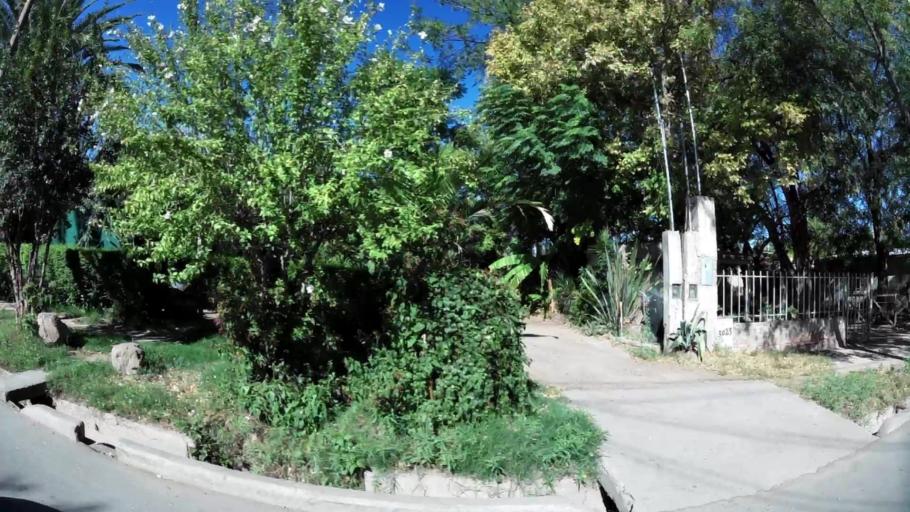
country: AR
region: Mendoza
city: Las Heras
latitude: -32.8364
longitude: -68.8295
